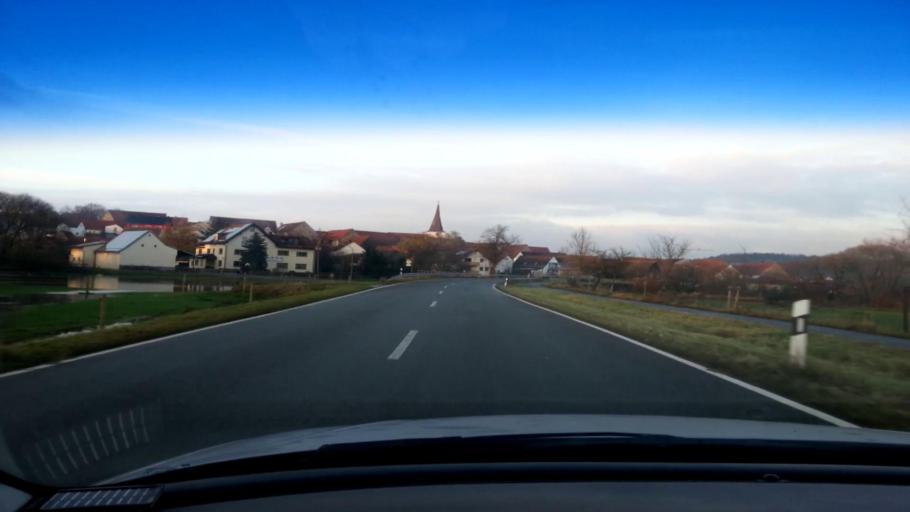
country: DE
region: Bavaria
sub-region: Upper Franconia
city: Frensdorf
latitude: 49.7897
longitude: 10.8869
